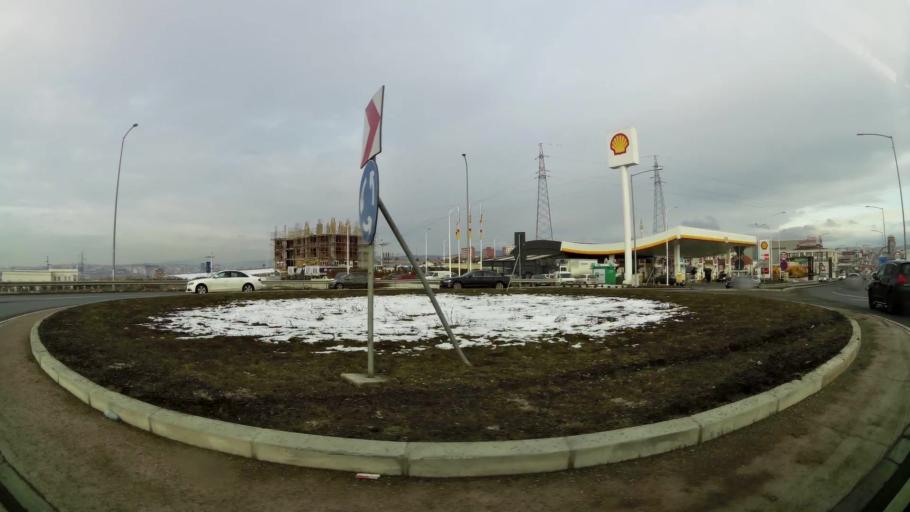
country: XK
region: Pristina
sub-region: Komuna e Prishtines
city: Pristina
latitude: 42.6316
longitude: 21.1445
